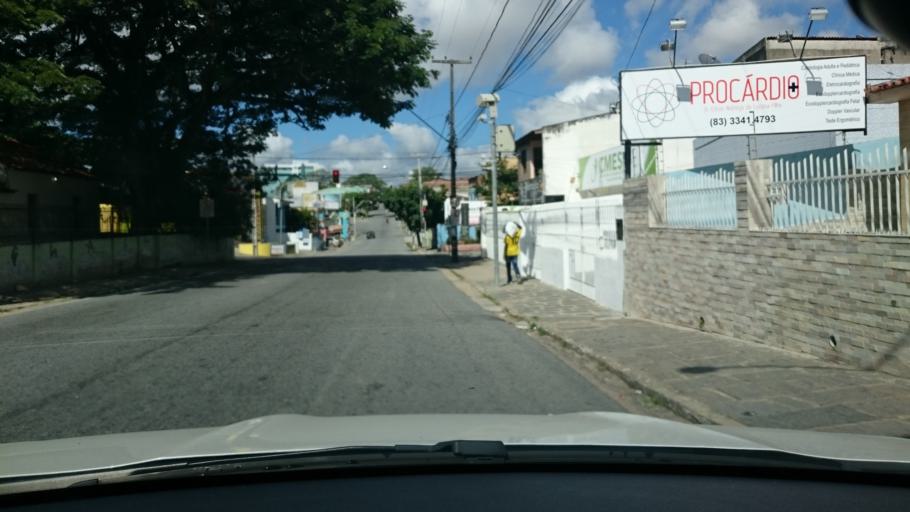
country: BR
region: Paraiba
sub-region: Campina Grande
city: Campina Grande
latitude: -7.2209
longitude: -35.8925
